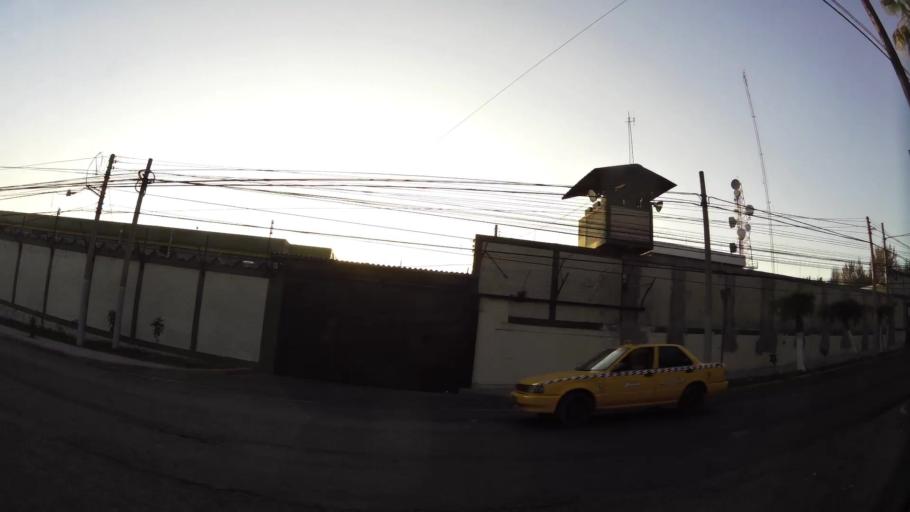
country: SV
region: La Libertad
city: Antiguo Cuscatlan
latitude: 13.6910
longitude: -89.2312
